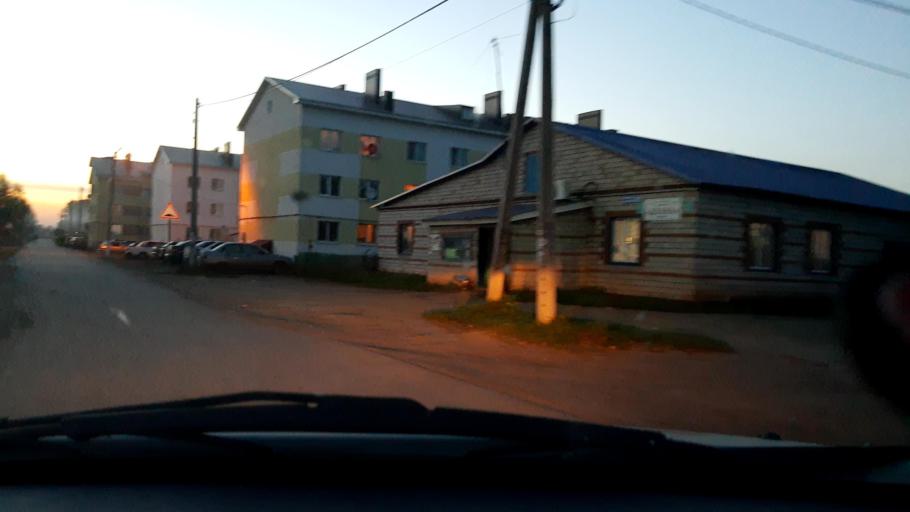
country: RU
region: Bashkortostan
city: Ulukulevo
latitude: 54.4216
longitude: 56.3430
